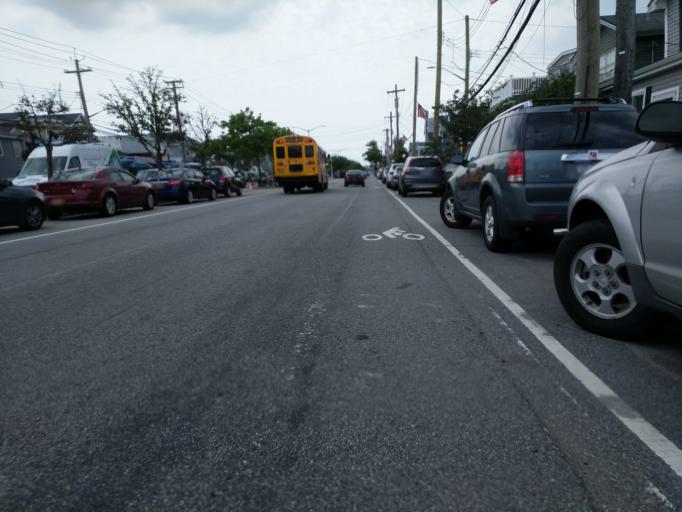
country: US
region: New York
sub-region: Nassau County
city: Inwood
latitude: 40.6042
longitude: -73.8200
